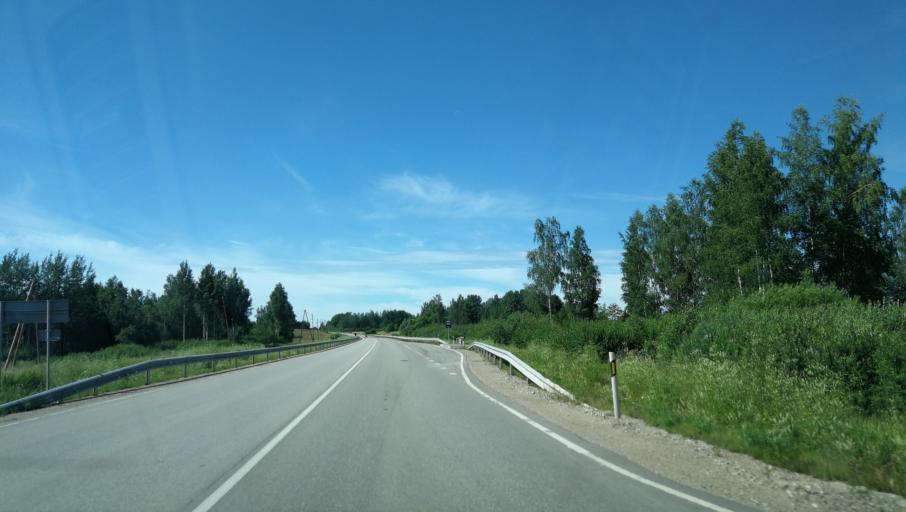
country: LV
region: Gulbenes Rajons
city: Gulbene
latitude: 57.1336
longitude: 26.6987
